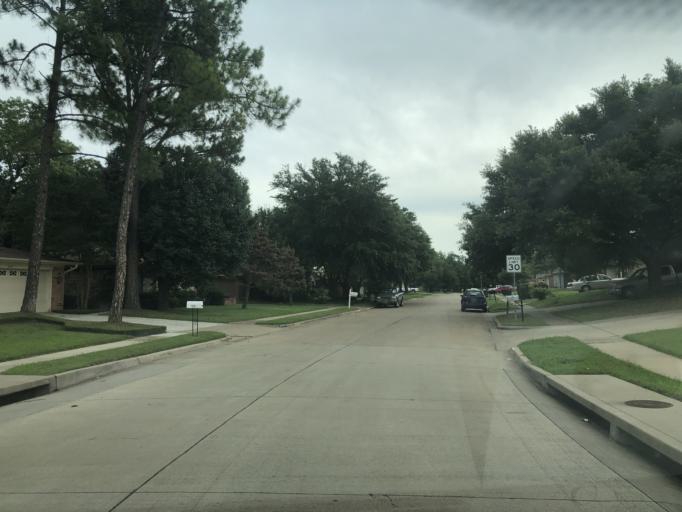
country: US
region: Texas
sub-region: Dallas County
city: Irving
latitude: 32.7858
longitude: -96.9767
